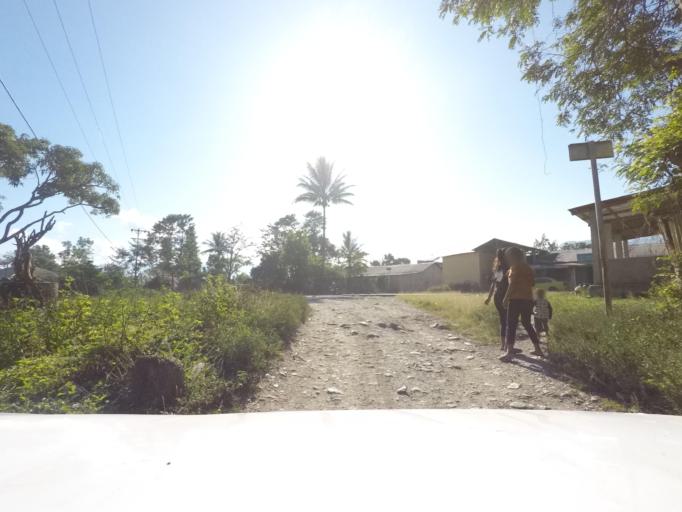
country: TL
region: Ermera
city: Gleno
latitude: -8.7282
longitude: 125.4299
